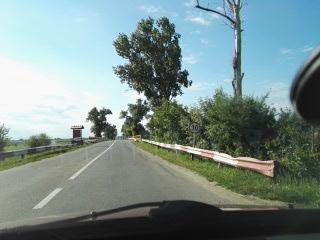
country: RO
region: Giurgiu
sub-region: Comuna Comana
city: Comana
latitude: 44.1774
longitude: 26.1415
